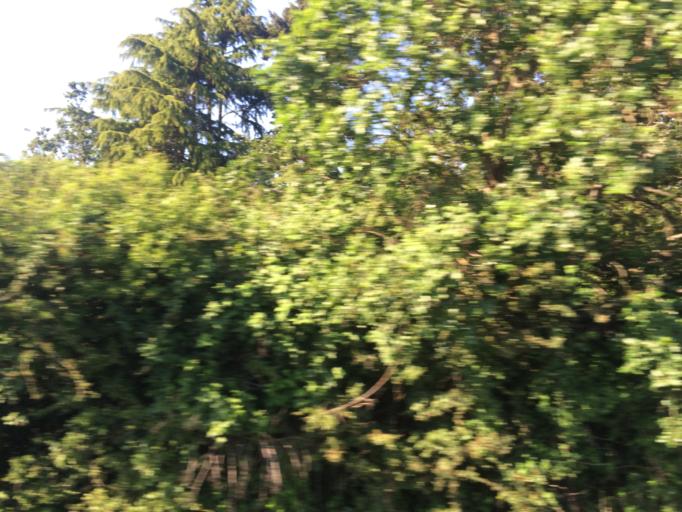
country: CA
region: British Columbia
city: Victoria
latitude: 48.4589
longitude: -123.4003
